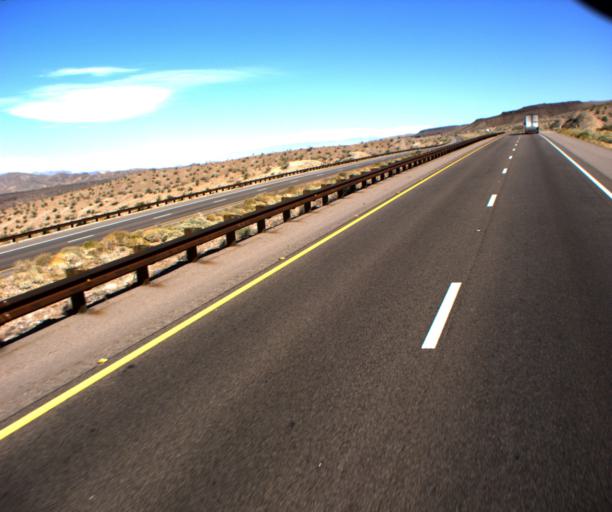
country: US
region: Nevada
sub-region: Clark County
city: Boulder City
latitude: 35.9266
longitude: -114.6333
